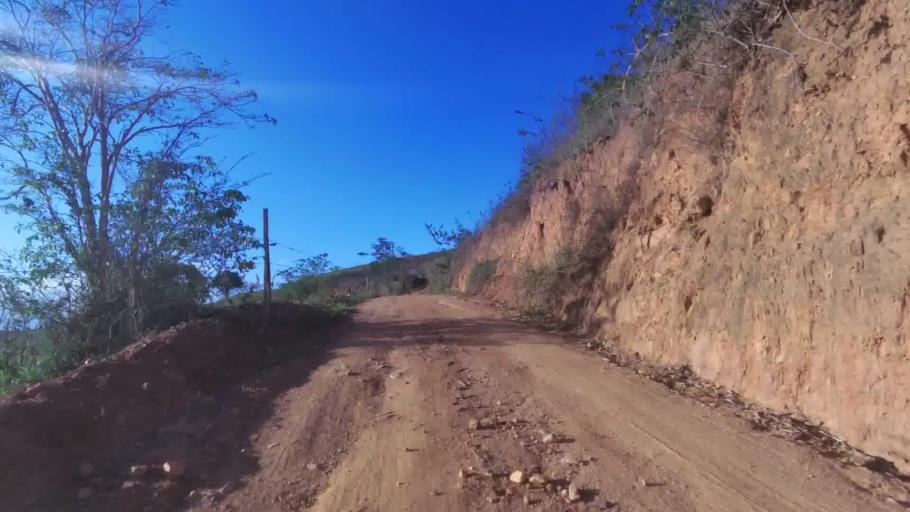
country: BR
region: Espirito Santo
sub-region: Marataizes
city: Marataizes
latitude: -21.1592
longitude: -41.0354
